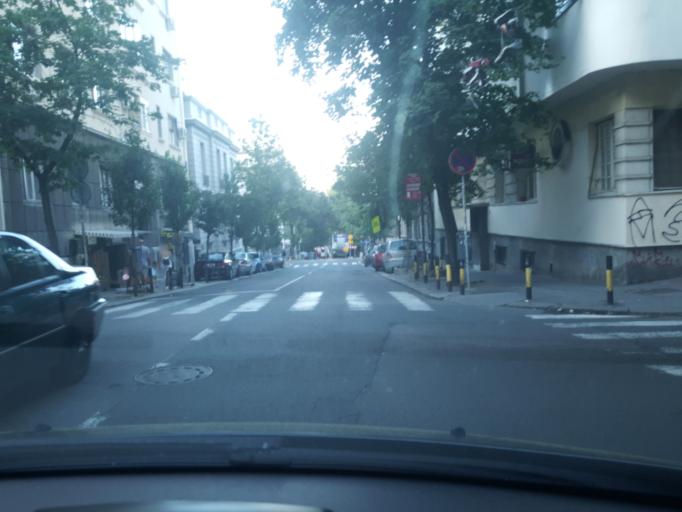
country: RS
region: Central Serbia
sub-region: Belgrade
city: Stari Grad
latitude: 44.8180
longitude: 20.4608
